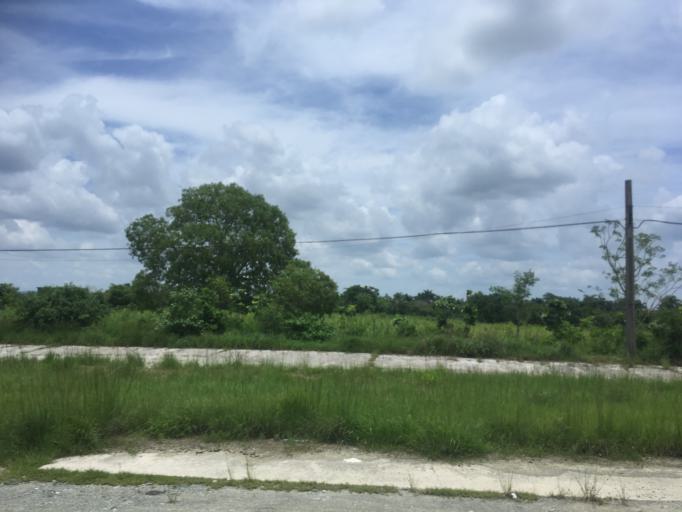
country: CU
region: Villa Clara
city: Esperanza
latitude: 22.4304
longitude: -80.0539
